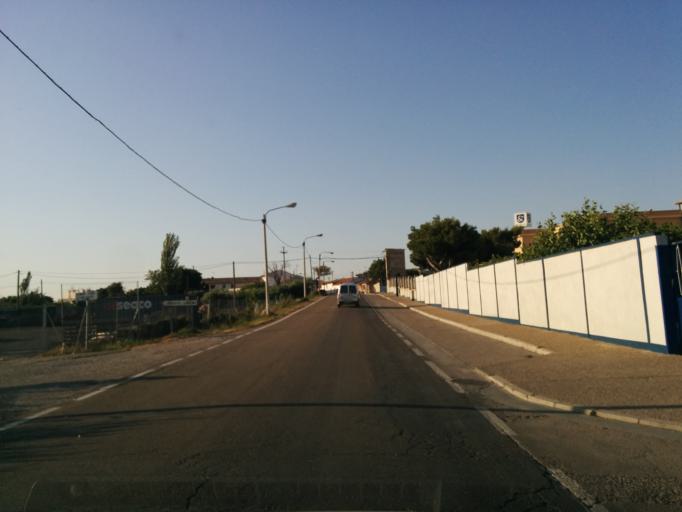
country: ES
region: Aragon
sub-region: Provincia de Zaragoza
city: Zaragoza
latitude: 41.6593
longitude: -0.8363
